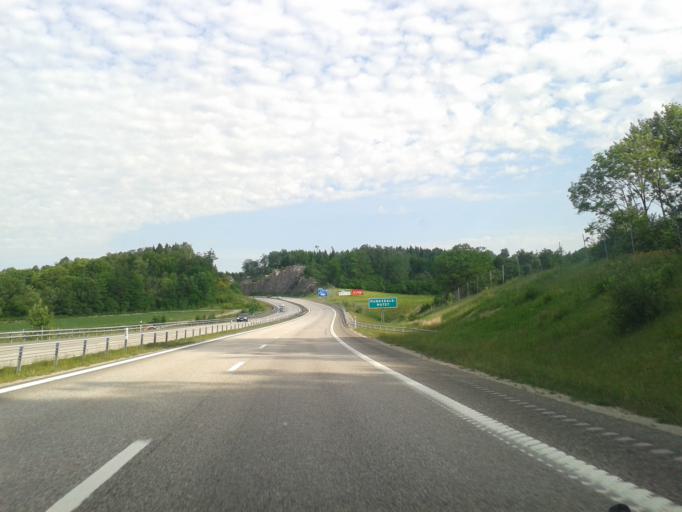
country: SE
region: Vaestra Goetaland
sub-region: Munkedals Kommun
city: Munkedal
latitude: 58.4513
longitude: 11.6691
